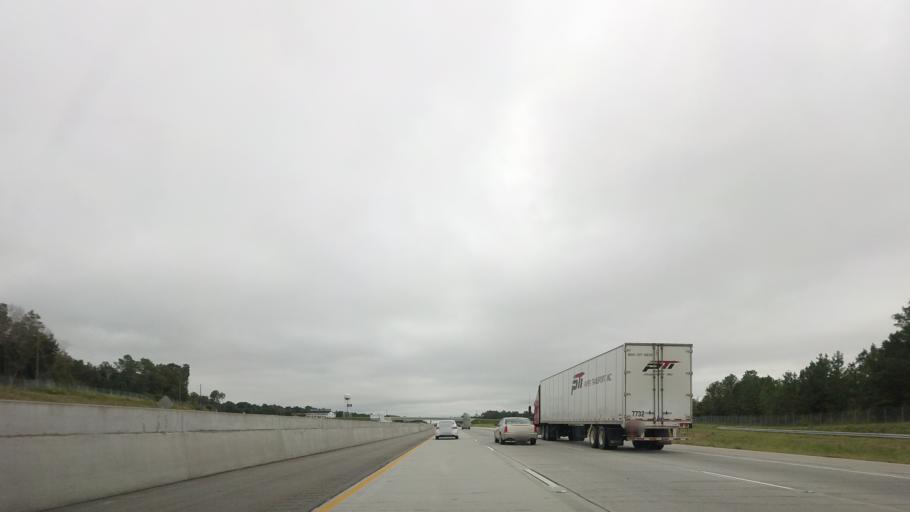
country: US
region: Georgia
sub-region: Tift County
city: Unionville
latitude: 31.3627
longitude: -83.4914
